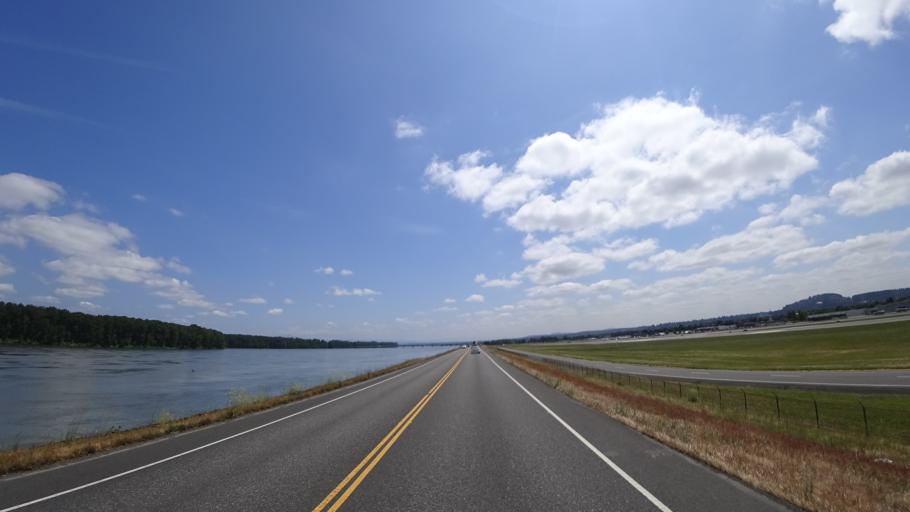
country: US
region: Washington
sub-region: Clark County
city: Orchards
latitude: 45.5873
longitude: -122.5707
